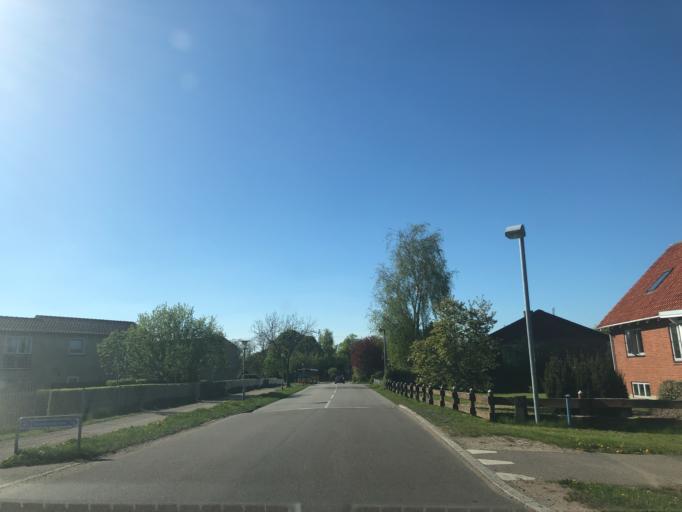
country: DK
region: Zealand
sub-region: Koge Kommune
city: Bjaeverskov
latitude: 55.4581
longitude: 12.0251
